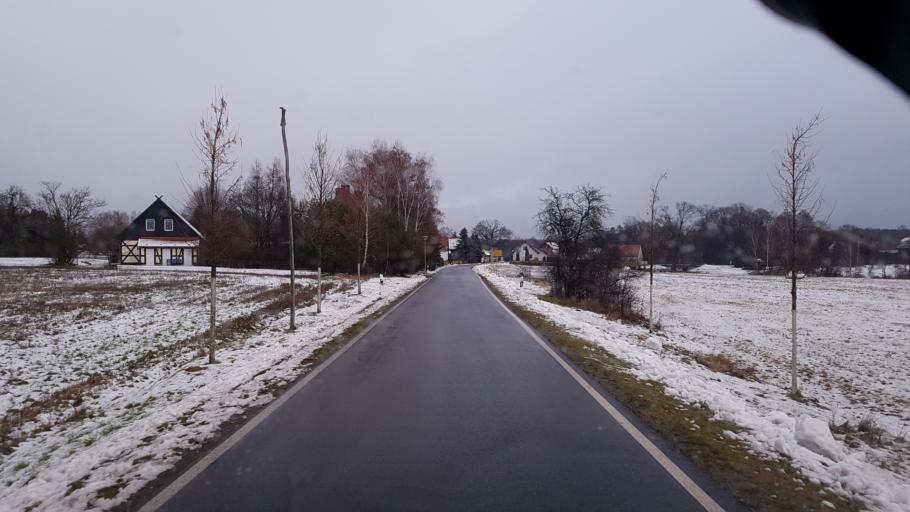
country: DE
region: Brandenburg
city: Neu Zauche
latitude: 51.9599
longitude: 14.1306
